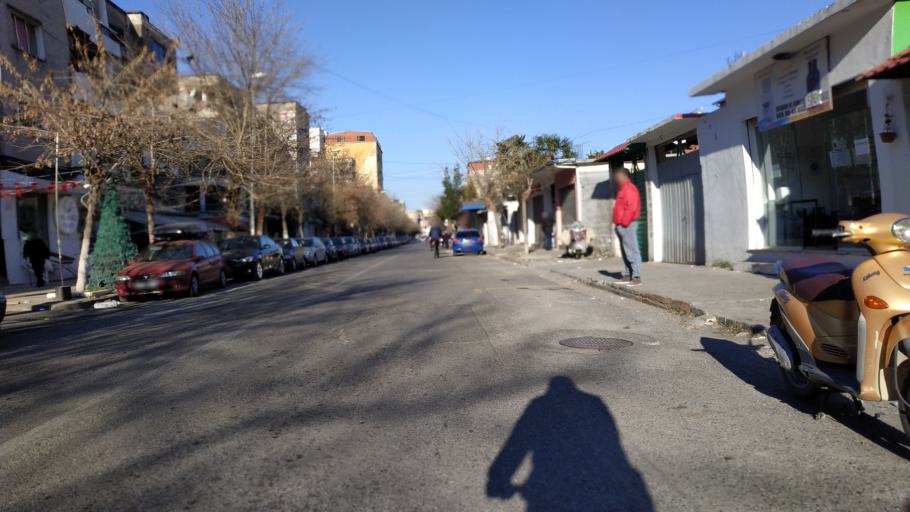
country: AL
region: Shkoder
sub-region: Rrethi i Shkodres
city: Shkoder
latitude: 42.0624
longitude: 19.5114
